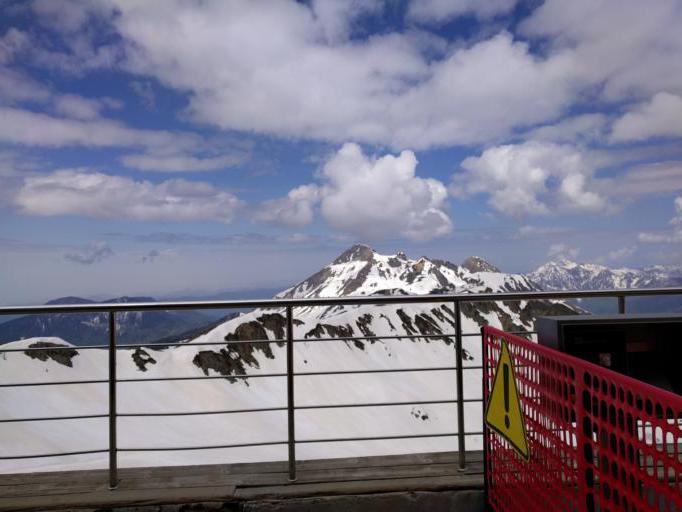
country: RU
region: Krasnodarskiy
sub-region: Sochi City
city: Krasnaya Polyana
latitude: 43.6252
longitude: 40.3101
